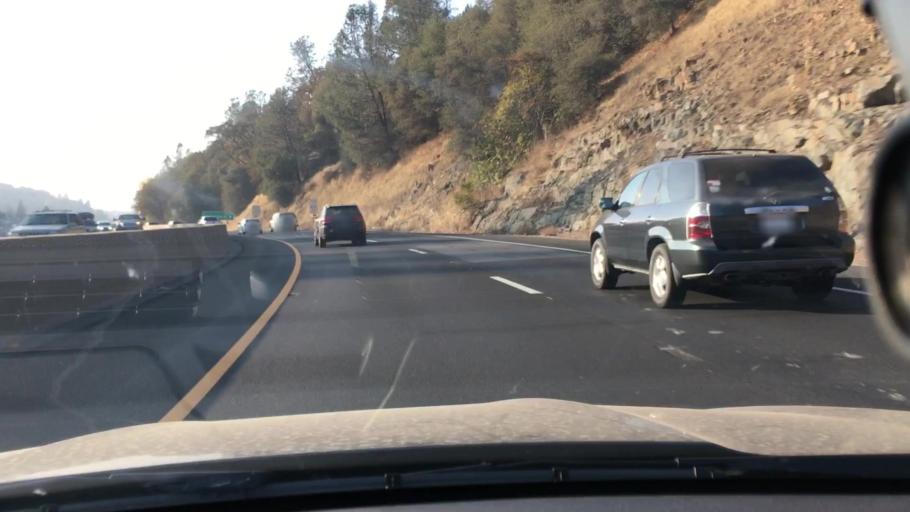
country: US
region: California
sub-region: El Dorado County
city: Placerville
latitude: 38.7296
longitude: -120.8104
